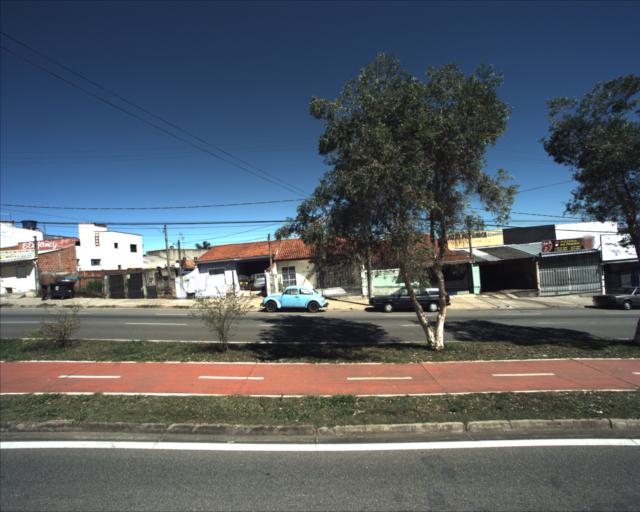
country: BR
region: Sao Paulo
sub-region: Sorocaba
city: Sorocaba
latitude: -23.4899
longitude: -47.4880
